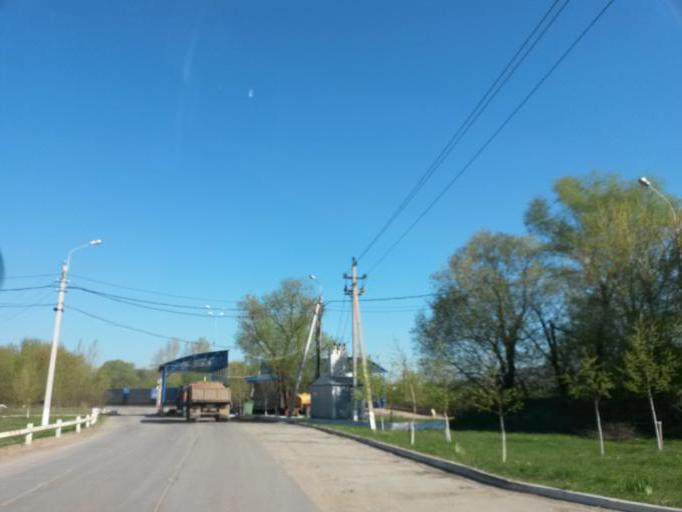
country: RU
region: Moskovskaya
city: Alekseyevka
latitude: 55.6155
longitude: 37.7934
